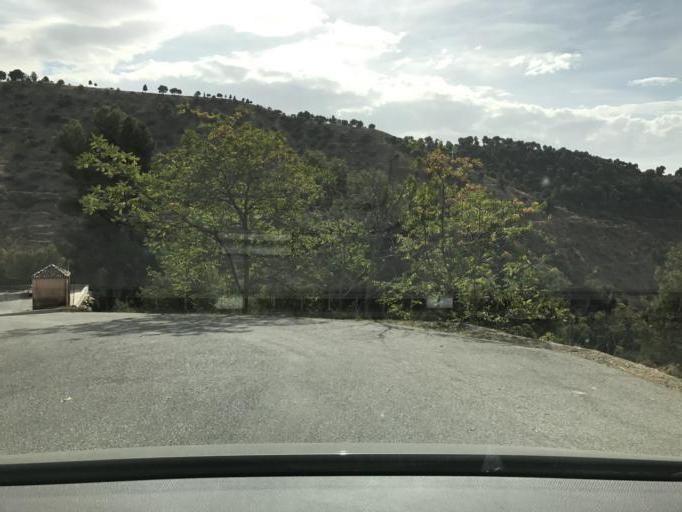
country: ES
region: Andalusia
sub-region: Provincia de Granada
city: Granada
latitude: 37.1836
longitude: -3.5785
